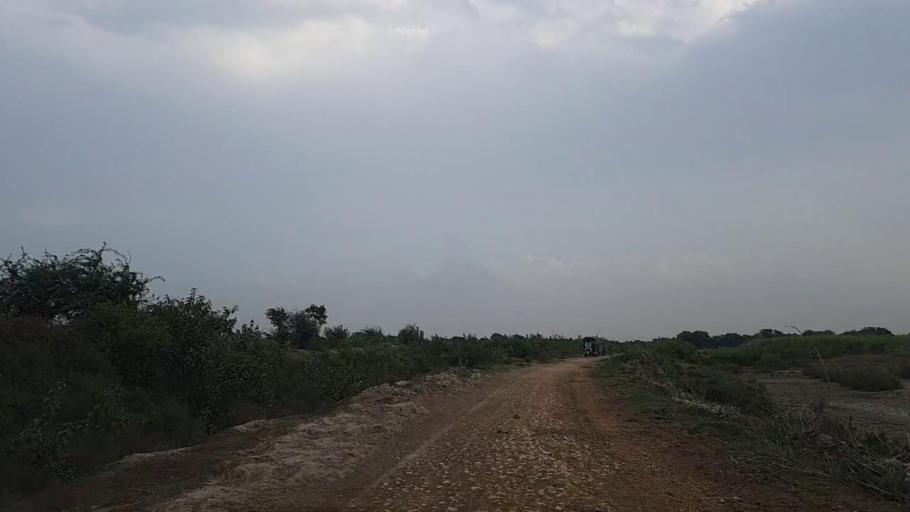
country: PK
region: Sindh
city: Daro Mehar
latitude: 24.7595
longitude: 68.1570
